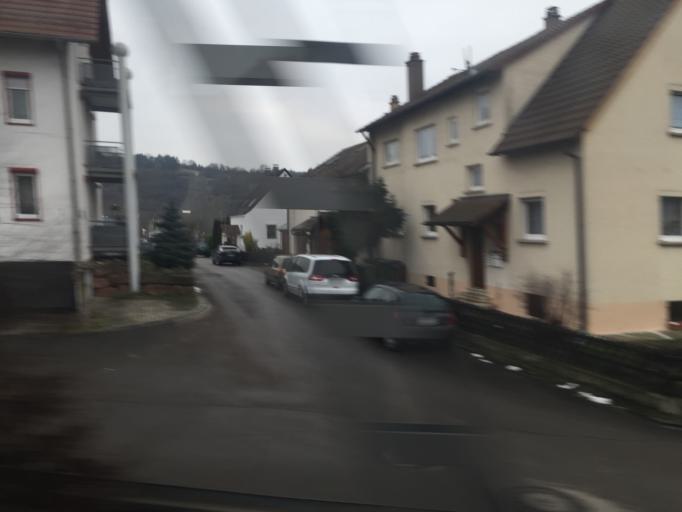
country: DE
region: Baden-Wuerttemberg
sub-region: Regierungsbezirk Stuttgart
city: Walheim
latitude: 49.0139
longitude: 9.1542
